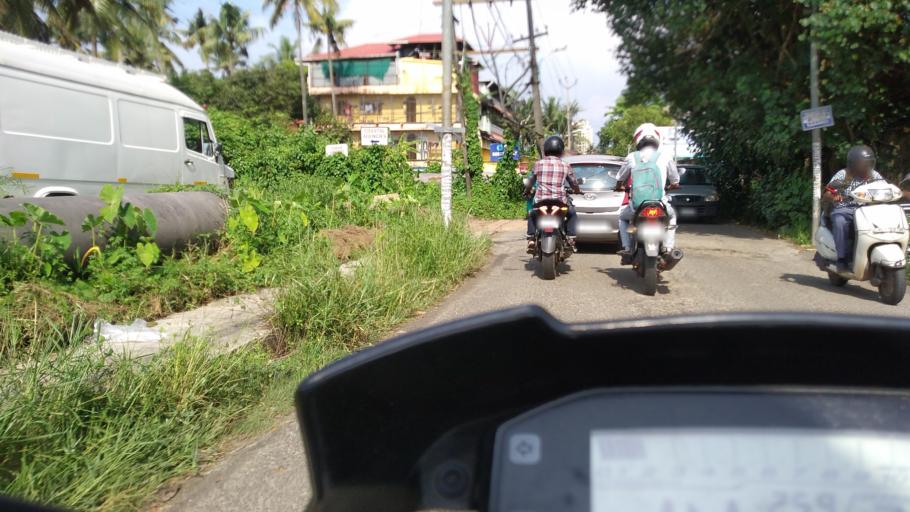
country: IN
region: Kerala
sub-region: Ernakulam
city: Cochin
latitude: 9.9831
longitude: 76.2922
